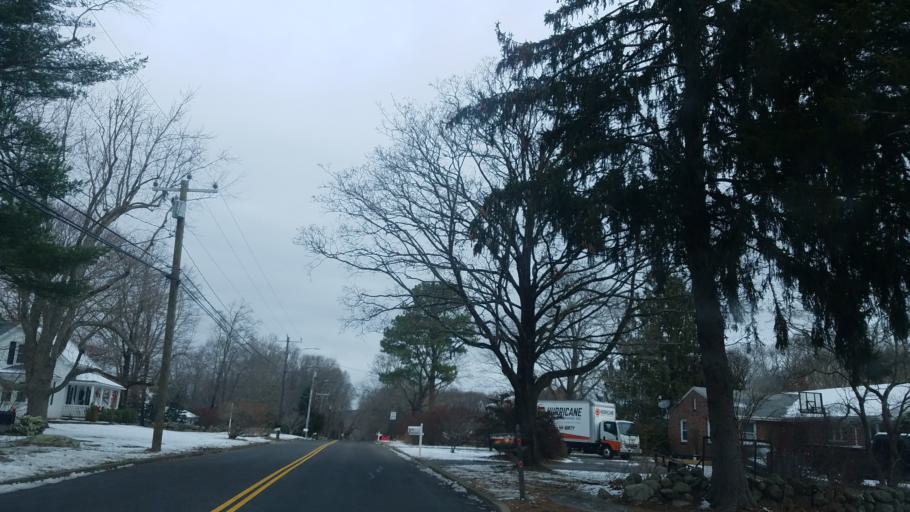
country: US
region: Connecticut
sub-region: New London County
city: Central Waterford
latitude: 41.3432
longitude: -72.1549
